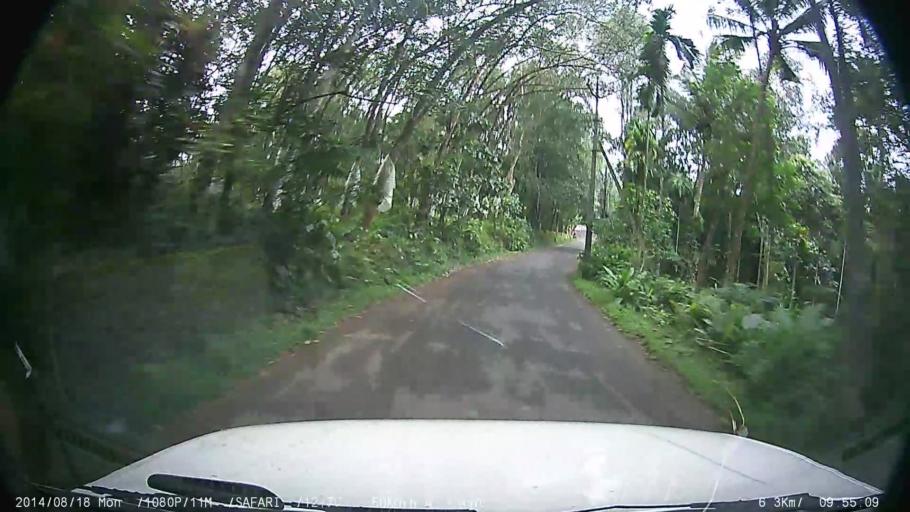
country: IN
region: Kerala
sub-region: Kottayam
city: Palackattumala
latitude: 9.7678
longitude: 76.5633
